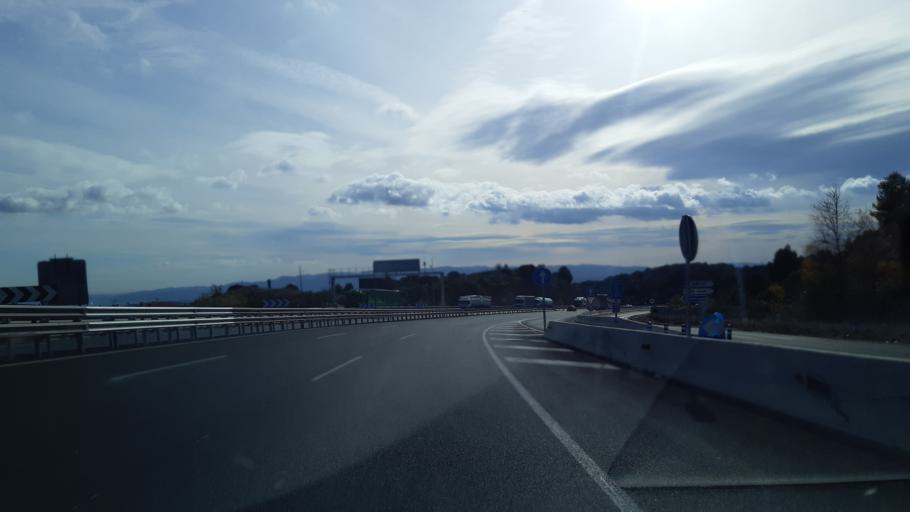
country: ES
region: Catalonia
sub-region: Provincia de Barcelona
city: Collbato
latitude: 41.5900
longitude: 1.7724
